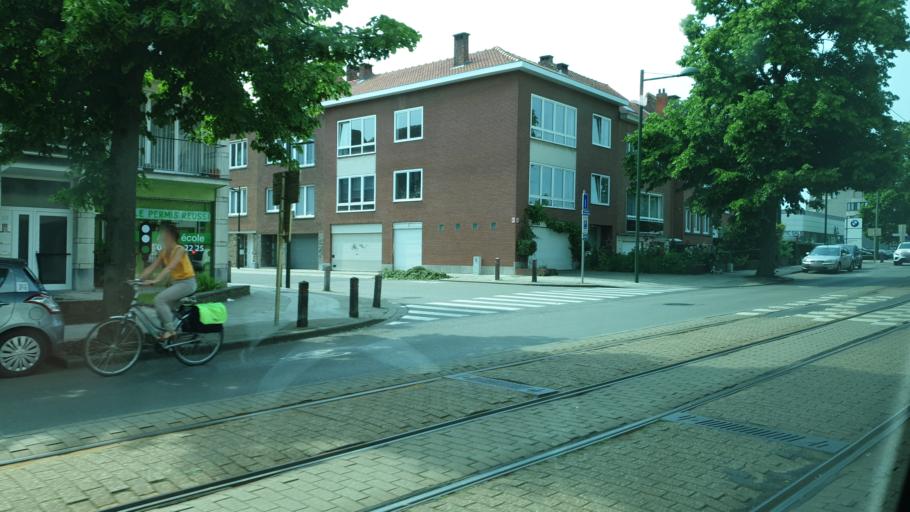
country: BE
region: Flanders
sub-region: Provincie Vlaams-Brabant
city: Kraainem
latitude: 50.8425
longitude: 4.4650
